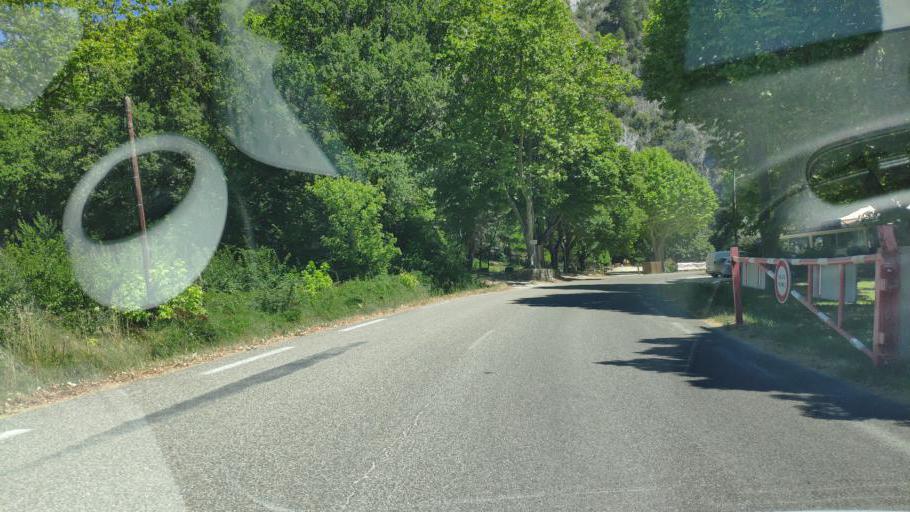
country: FR
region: Provence-Alpes-Cote d'Azur
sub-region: Departement du Vaucluse
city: Malaucene
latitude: 44.1675
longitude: 5.1480
